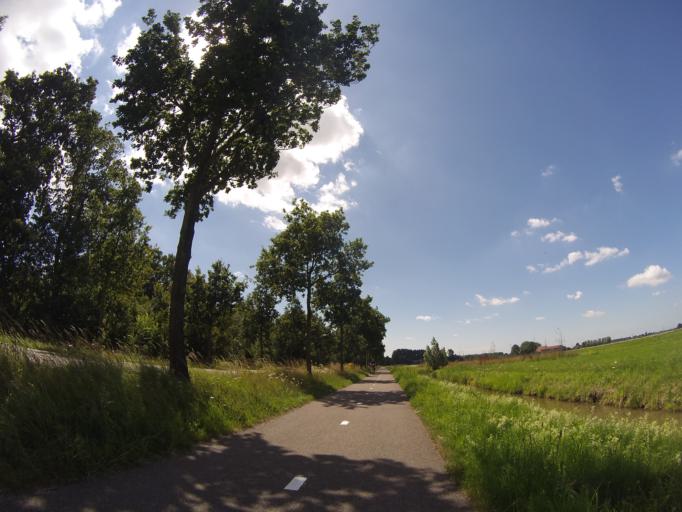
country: NL
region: Utrecht
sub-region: Stichtse Vecht
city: Spechtenkamp
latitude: 52.1275
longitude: 4.9841
